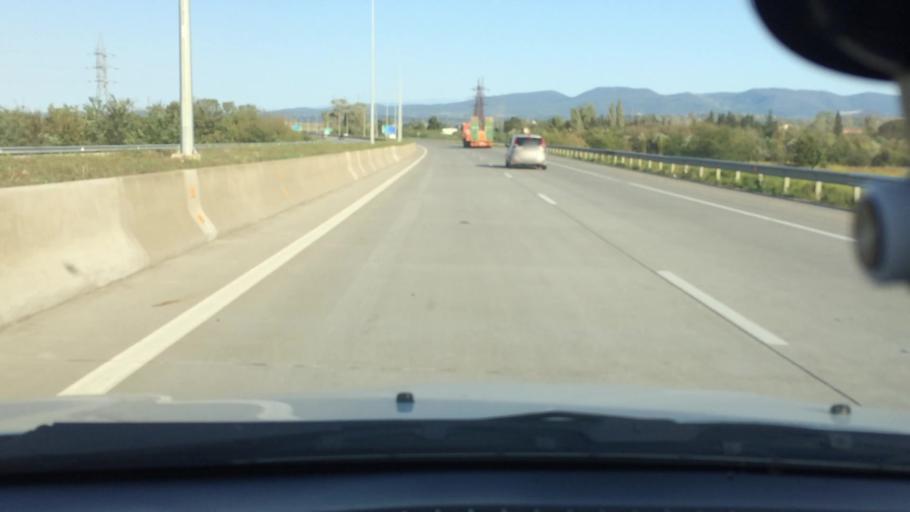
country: GE
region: Imereti
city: Zestap'oni
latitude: 42.1524
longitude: 42.9592
